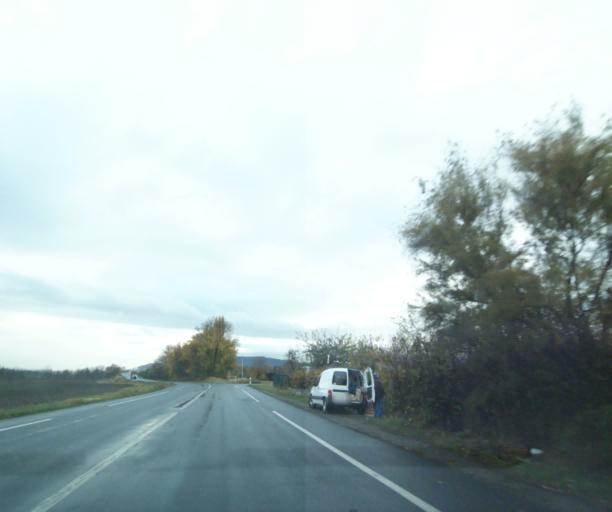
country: FR
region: Auvergne
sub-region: Departement du Puy-de-Dome
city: Aulnat
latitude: 45.7764
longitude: 3.1476
